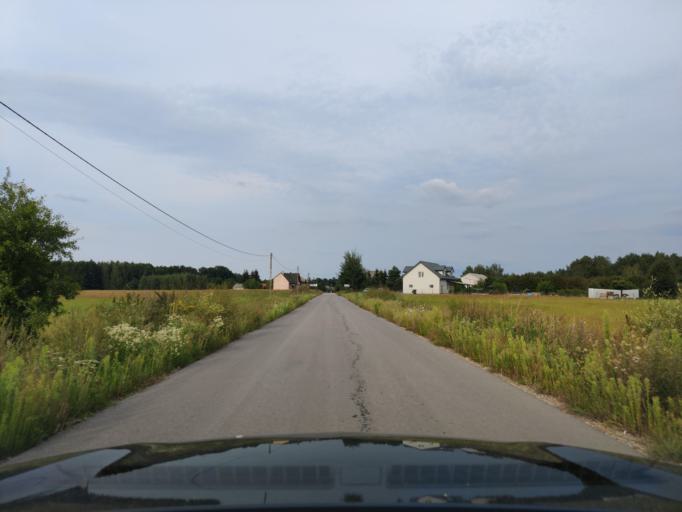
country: PL
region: Masovian Voivodeship
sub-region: Powiat pultuski
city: Obryte
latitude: 52.7088
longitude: 21.2343
